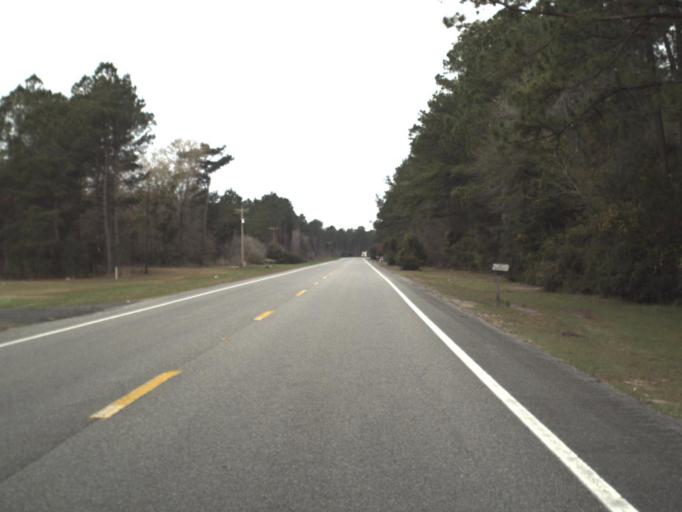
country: US
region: Florida
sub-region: Jefferson County
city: Monticello
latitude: 30.4945
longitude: -83.7381
